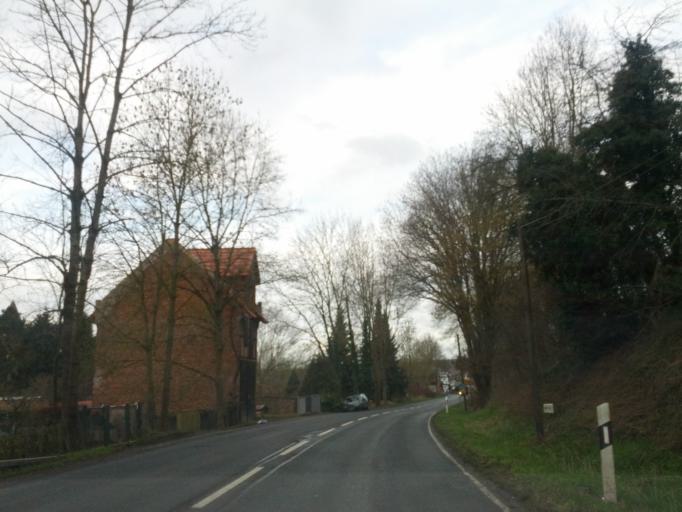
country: DE
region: Hesse
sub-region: Regierungsbezirk Kassel
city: Kaufungen
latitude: 51.2793
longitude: 9.6400
